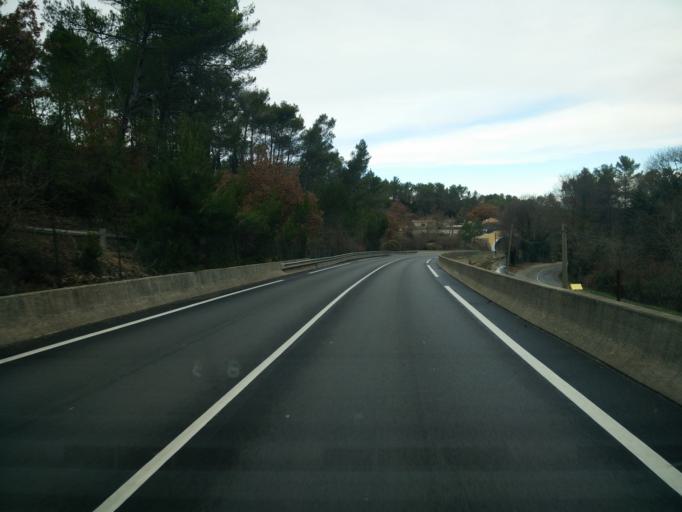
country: FR
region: Provence-Alpes-Cote d'Azur
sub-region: Departement du Var
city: La Celle
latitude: 43.3871
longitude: 6.0456
